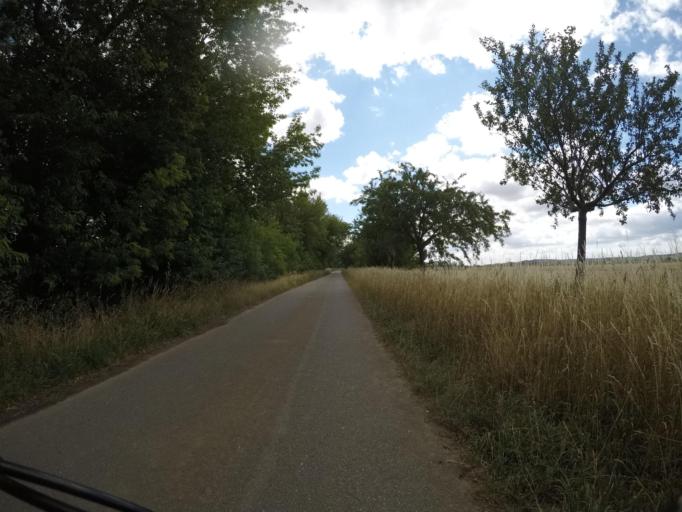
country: DE
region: Lower Saxony
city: Hitzacker
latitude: 53.2021
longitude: 11.0135
